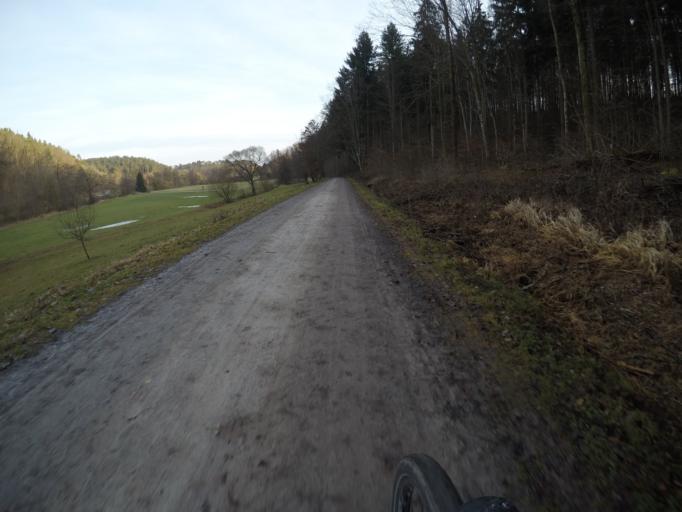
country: DE
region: Baden-Wuerttemberg
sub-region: Regierungsbezirk Stuttgart
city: Steinenbronn
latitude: 48.6442
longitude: 9.1070
